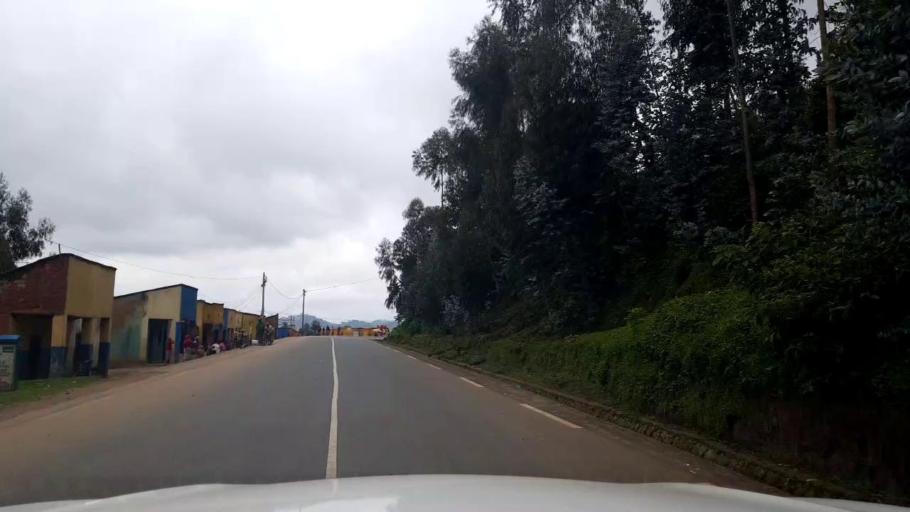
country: RW
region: Northern Province
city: Musanze
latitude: -1.6461
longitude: 29.5051
